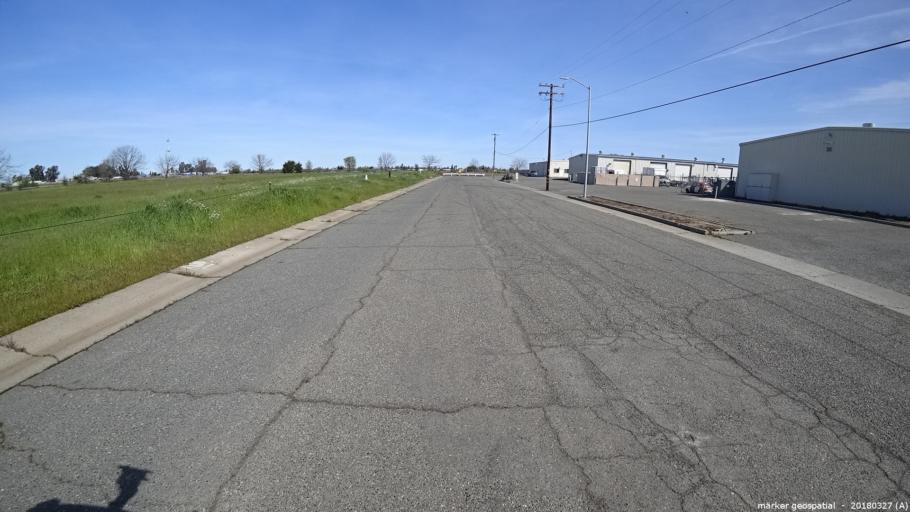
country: US
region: California
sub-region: Sacramento County
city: Rosemont
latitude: 38.5258
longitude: -121.3547
